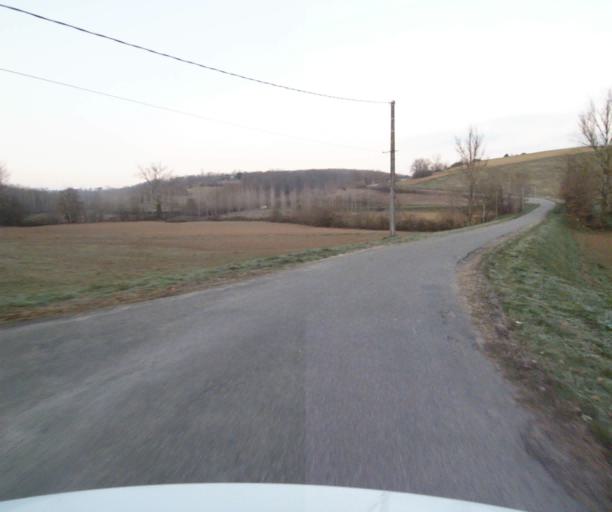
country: FR
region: Midi-Pyrenees
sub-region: Departement du Tarn-et-Garonne
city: Moissac
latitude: 44.1208
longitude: 1.0466
